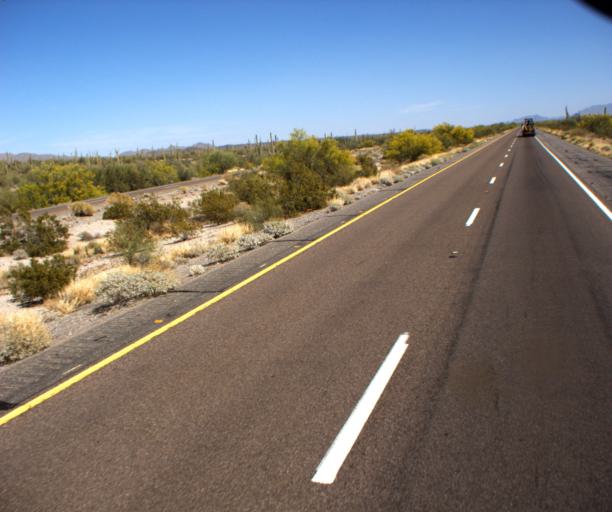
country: US
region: Arizona
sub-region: Maricopa County
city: Gila Bend
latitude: 32.8631
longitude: -112.4059
